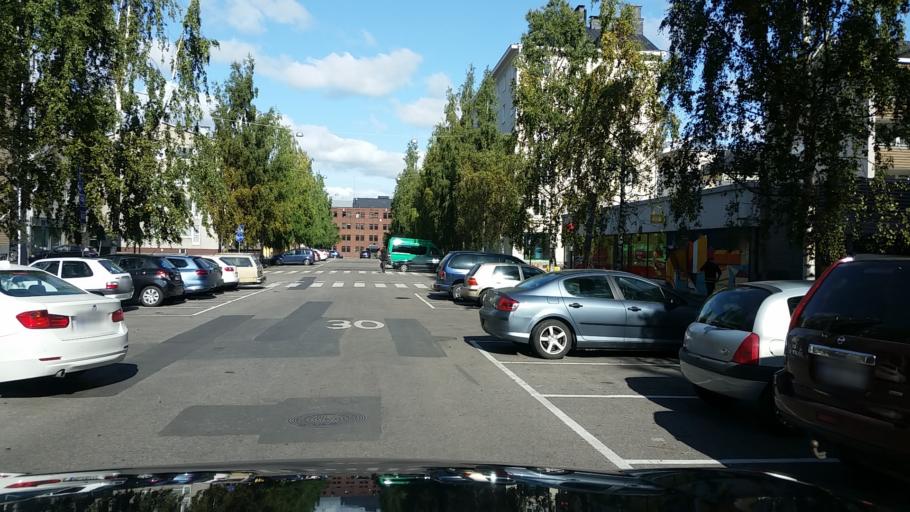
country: FI
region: Uusimaa
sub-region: Helsinki
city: Helsinki
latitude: 60.1915
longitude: 24.9421
